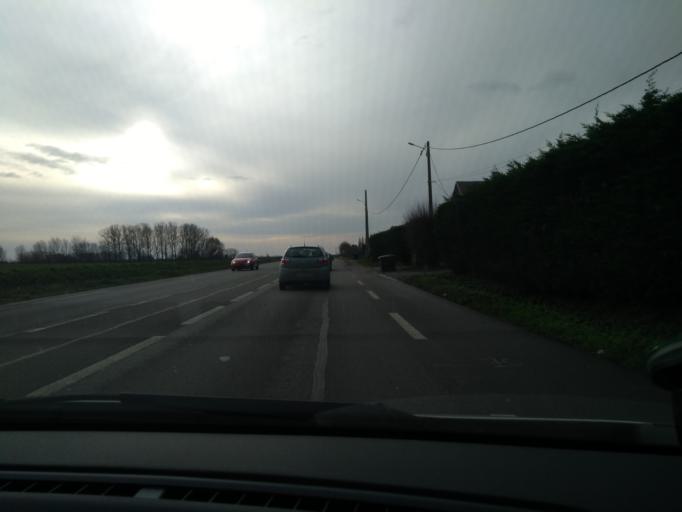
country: FR
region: Nord-Pas-de-Calais
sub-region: Departement du Nord
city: Maubeuge
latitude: 50.3258
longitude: 3.9749
